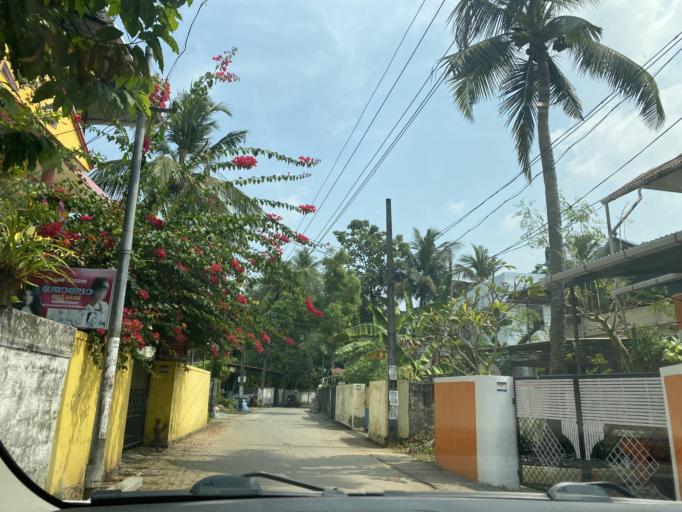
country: IN
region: Kerala
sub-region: Ernakulam
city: Cochin
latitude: 9.9411
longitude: 76.3089
